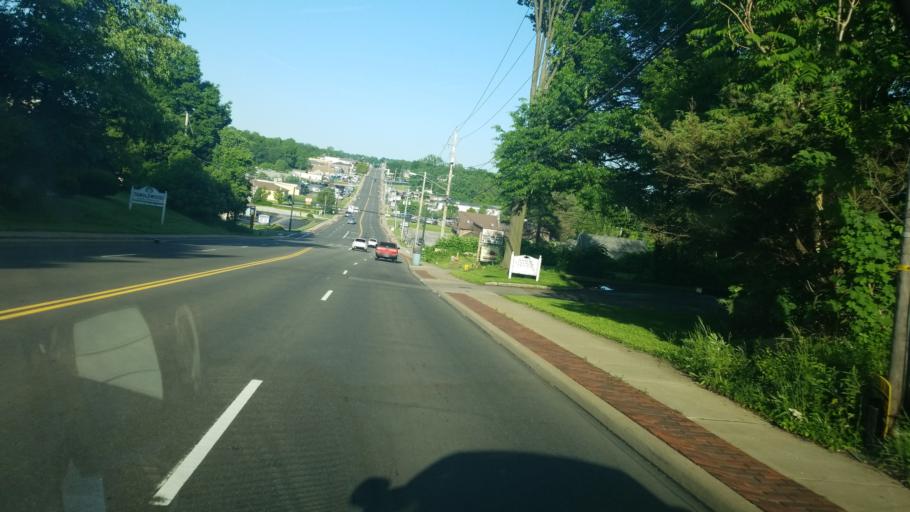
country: US
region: Ohio
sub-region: Summit County
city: Tallmadge
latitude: 41.1018
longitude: -81.4632
